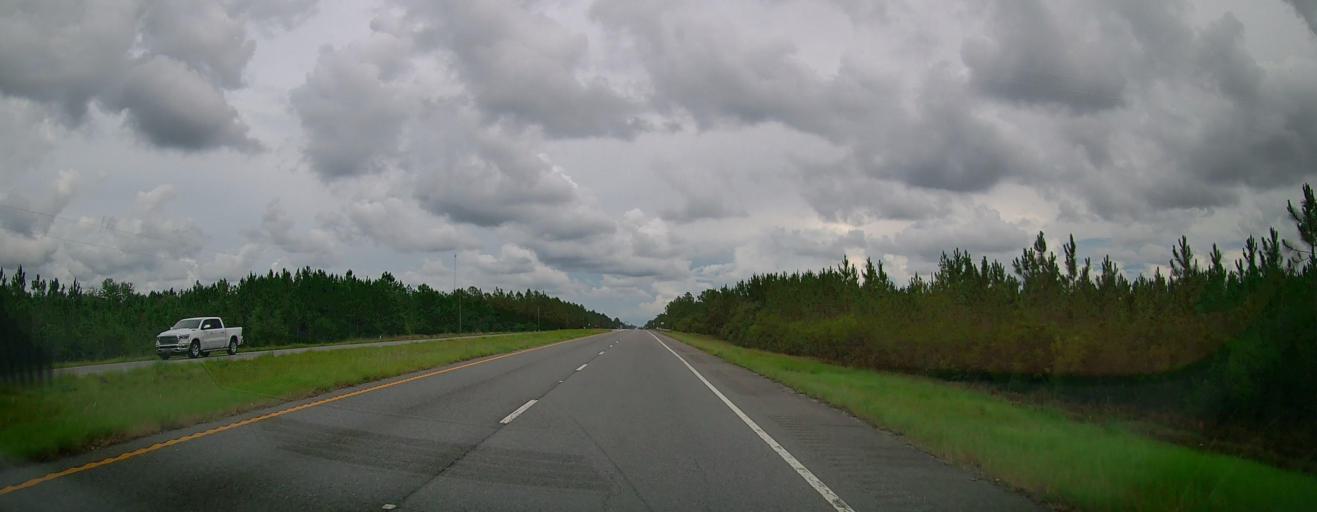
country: US
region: Georgia
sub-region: Wayne County
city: Jesup
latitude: 31.6872
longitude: -82.1136
